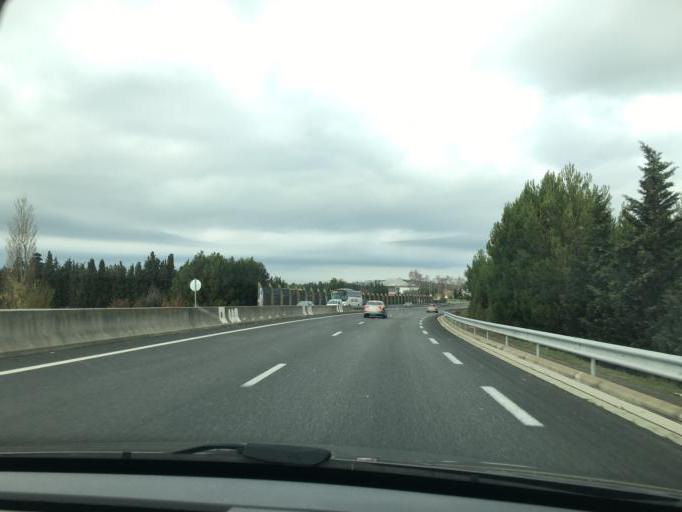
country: FR
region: Provence-Alpes-Cote d'Azur
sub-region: Departement des Bouches-du-Rhone
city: Noves
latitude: 43.9013
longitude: 4.8952
